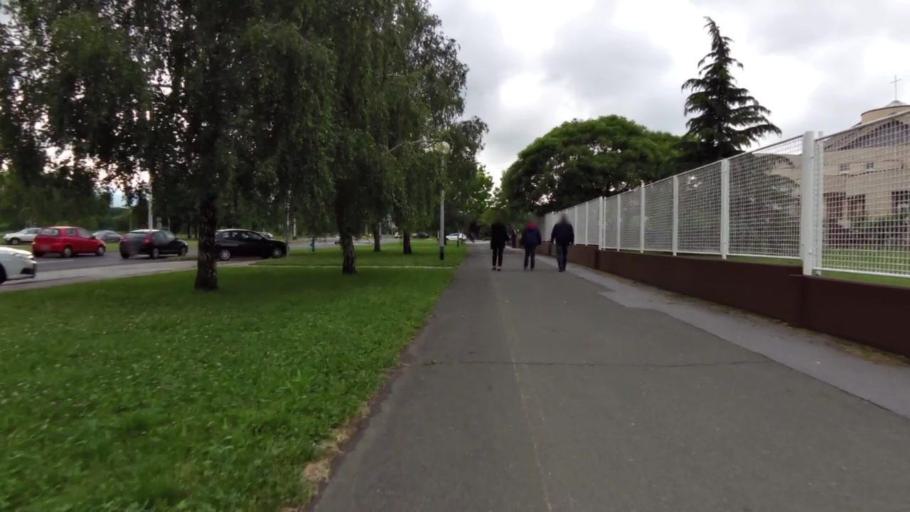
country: HR
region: Grad Zagreb
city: Dubrava
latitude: 45.8274
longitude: 16.0357
